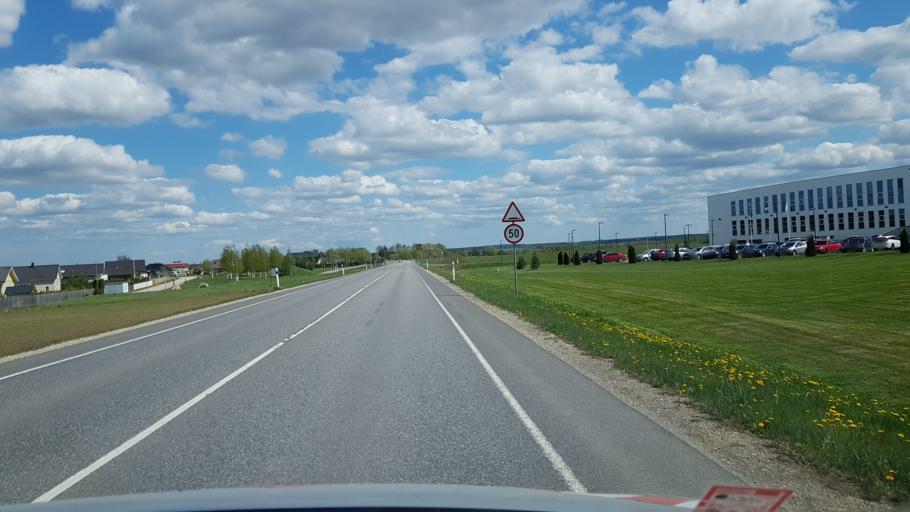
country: EE
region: Tartu
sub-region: UElenurme vald
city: Ulenurme
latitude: 58.3116
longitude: 26.6917
